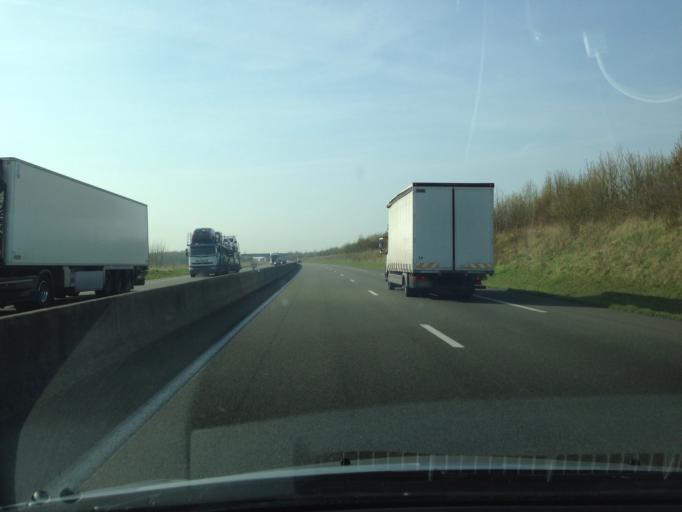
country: FR
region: Picardie
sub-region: Departement de la Somme
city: Sailly-Flibeaucourt
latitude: 50.1541
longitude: 1.7915
